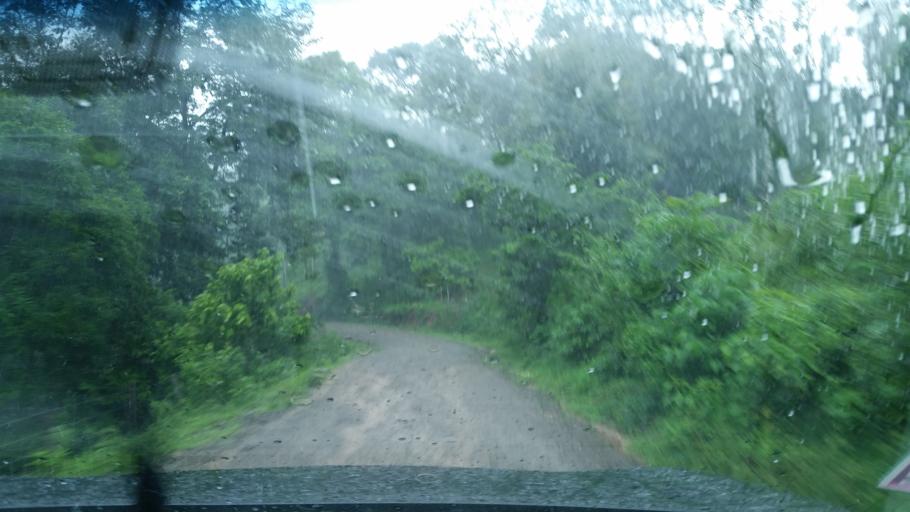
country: NI
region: Atlantico Norte (RAAN)
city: Waslala
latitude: 13.1596
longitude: -85.4235
